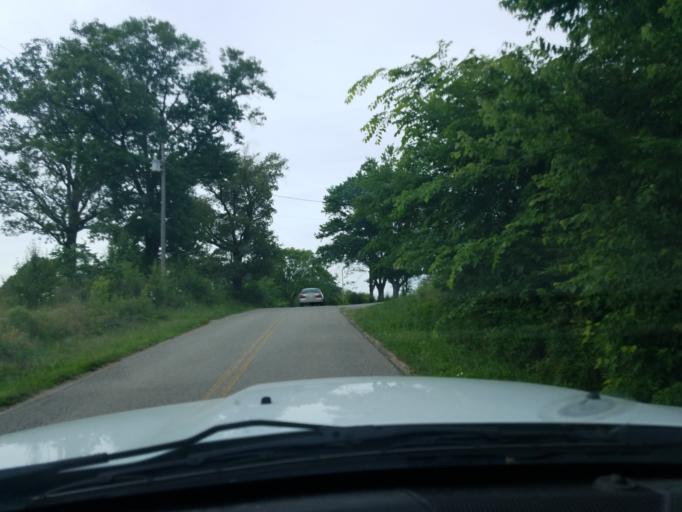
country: US
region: Tennessee
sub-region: Putnam County
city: Baxter
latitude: 36.1270
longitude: -85.5814
